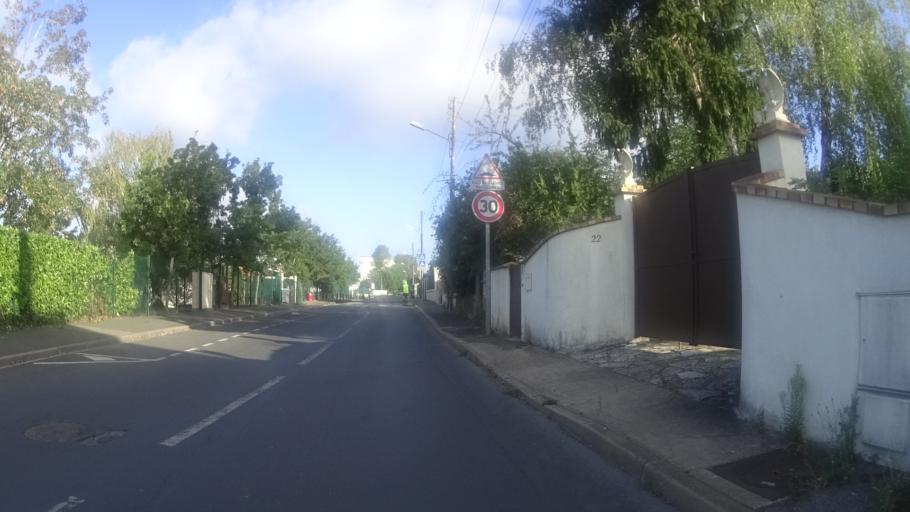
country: FR
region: Ile-de-France
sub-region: Departement de l'Essonne
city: Draveil
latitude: 48.6735
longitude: 2.4092
